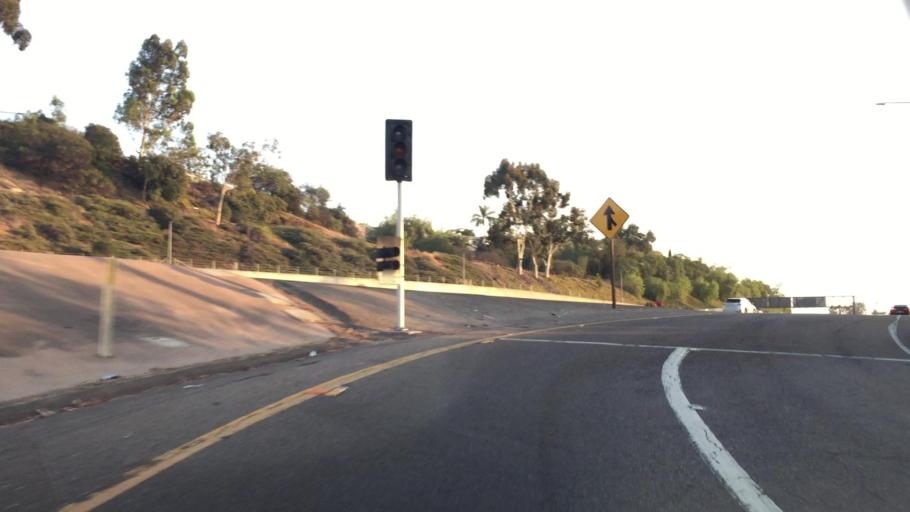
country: US
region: California
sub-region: San Diego County
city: La Mesa
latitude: 32.7744
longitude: -117.0135
